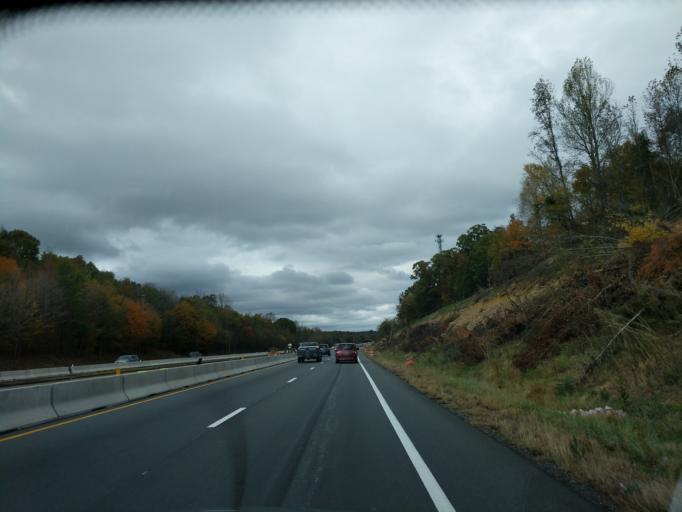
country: US
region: North Carolina
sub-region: Rowan County
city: Landis
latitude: 35.5179
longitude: -80.5696
